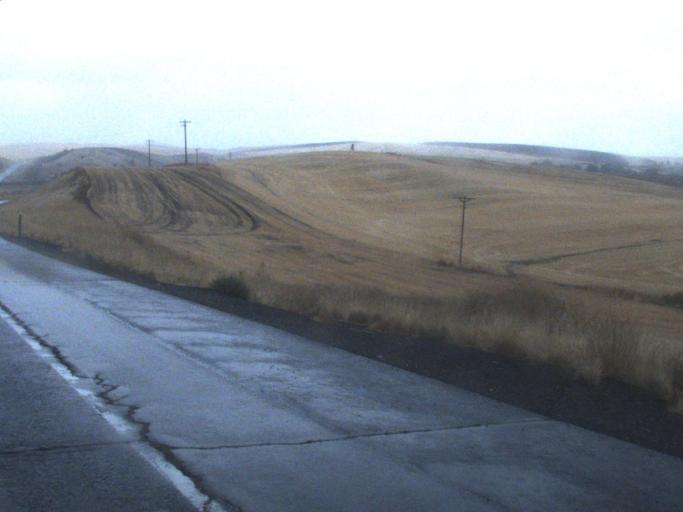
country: US
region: Washington
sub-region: Whitman County
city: Colfax
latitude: 47.2062
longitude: -117.3643
